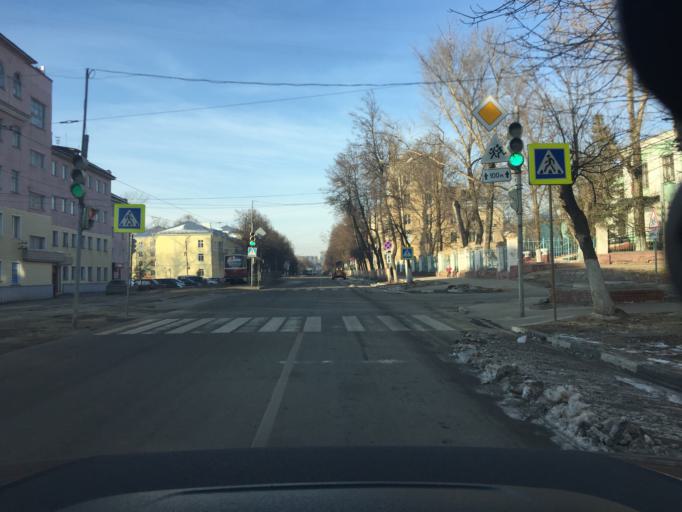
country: RU
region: Tula
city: Tula
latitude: 54.1790
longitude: 37.7081
